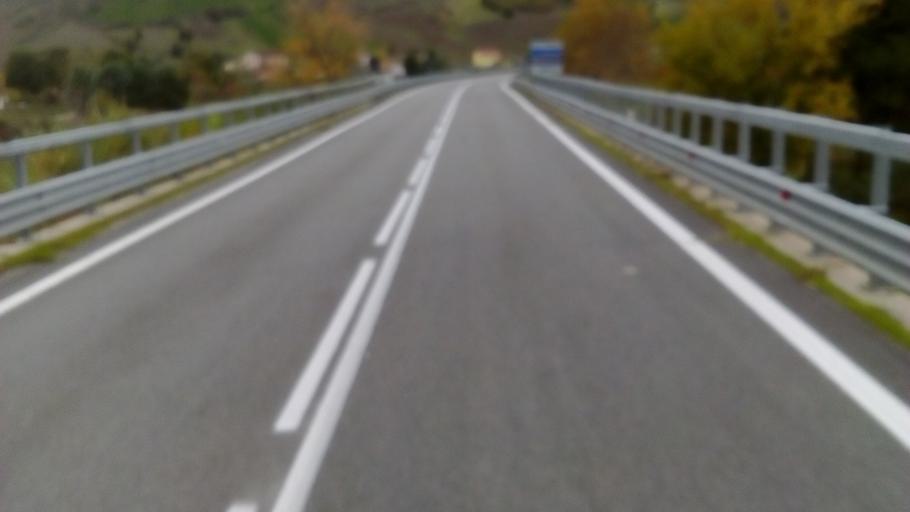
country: IT
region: Molise
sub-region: Provincia di Campobasso
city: Trivento
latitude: 41.8011
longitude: 14.5625
